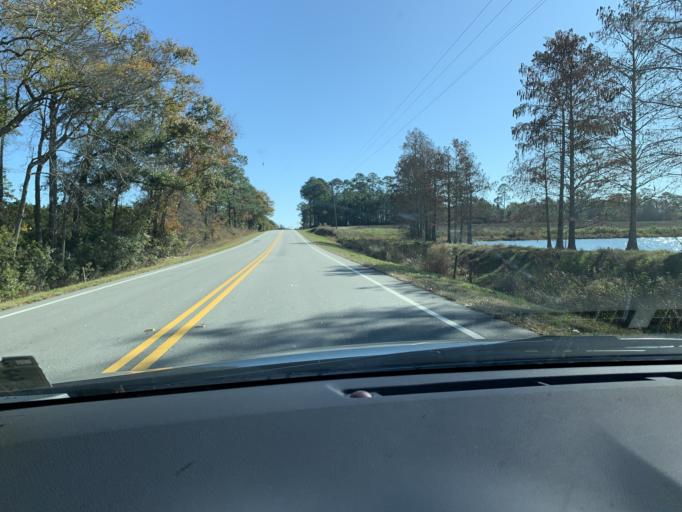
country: US
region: Georgia
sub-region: Ben Hill County
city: Fitzgerald
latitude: 31.7019
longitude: -83.1486
